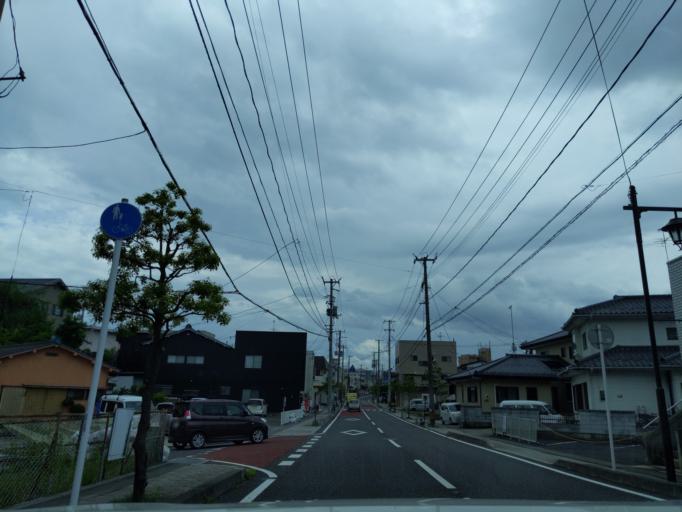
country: JP
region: Fukushima
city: Koriyama
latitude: 37.3899
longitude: 140.3717
